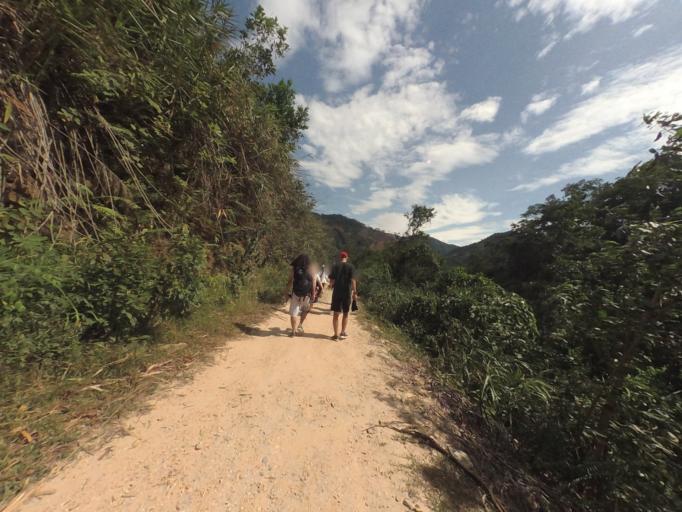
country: VN
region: Thua Thien-Hue
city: A Luoi
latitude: 16.3030
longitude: 107.3250
